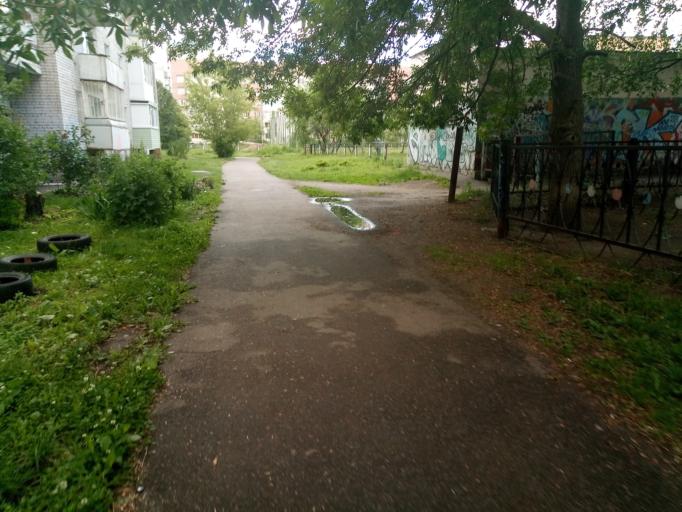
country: RU
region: Jaroslavl
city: Yaroslavl
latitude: 57.6432
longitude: 39.9547
